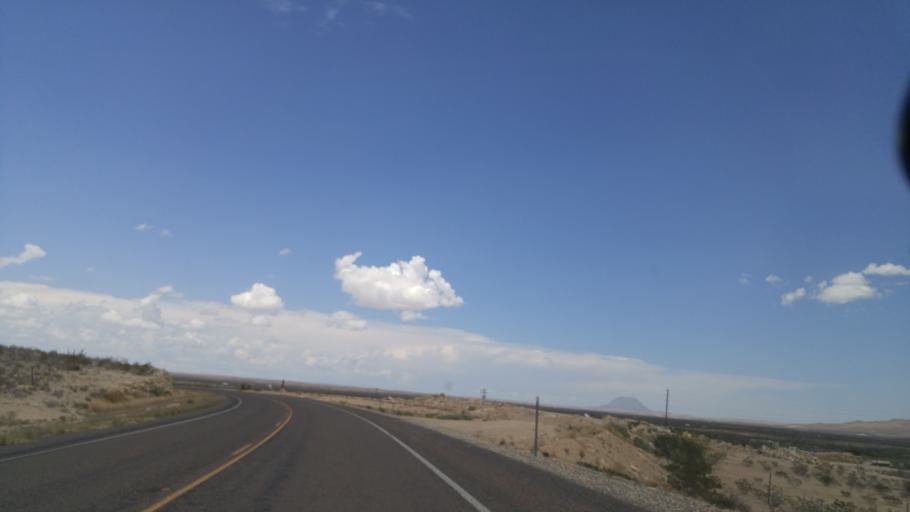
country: US
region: Texas
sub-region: Brewster County
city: Alpine
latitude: 29.5973
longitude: -103.5599
